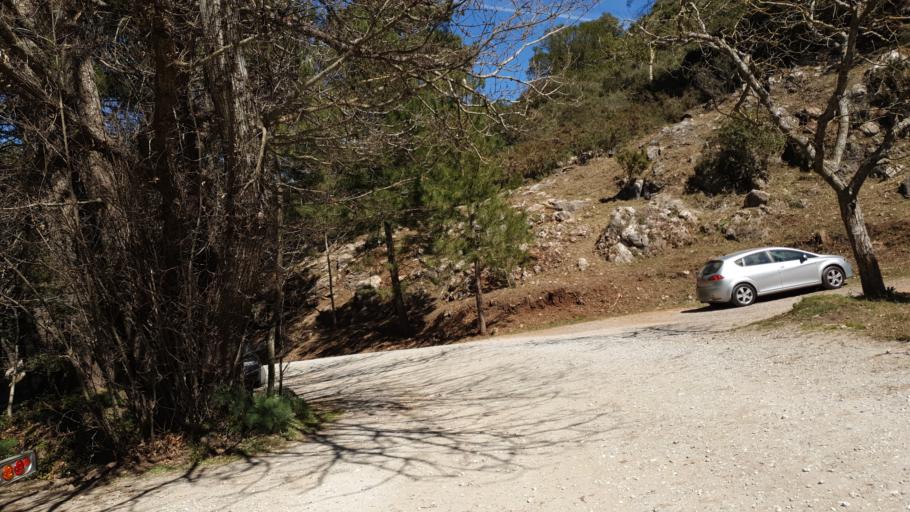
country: ES
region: Andalusia
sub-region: Provincia de Malaga
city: Ojen
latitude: 36.5783
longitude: -4.8842
